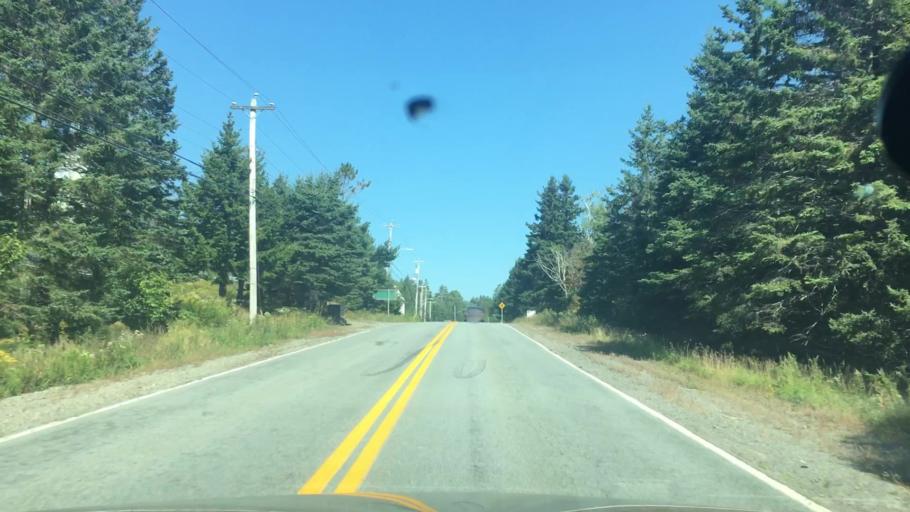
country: CA
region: Nova Scotia
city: New Glasgow
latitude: 44.9233
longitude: -62.5455
